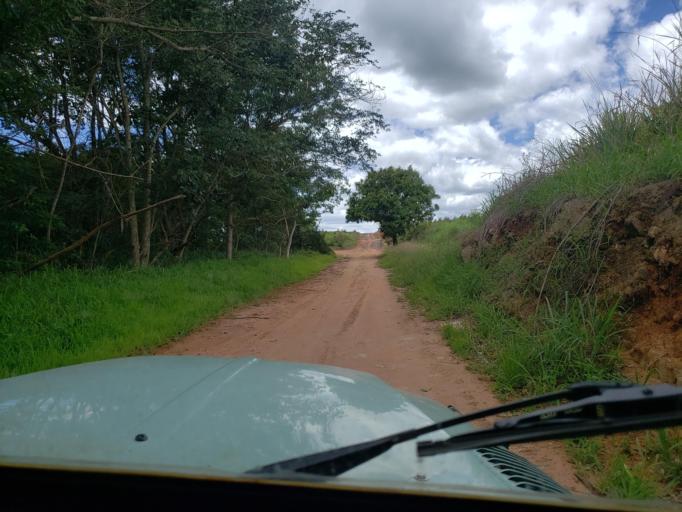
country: BR
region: Sao Paulo
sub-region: Santo Antonio Do Jardim
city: Espirito Santo do Pinhal
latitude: -22.1992
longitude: -46.8449
